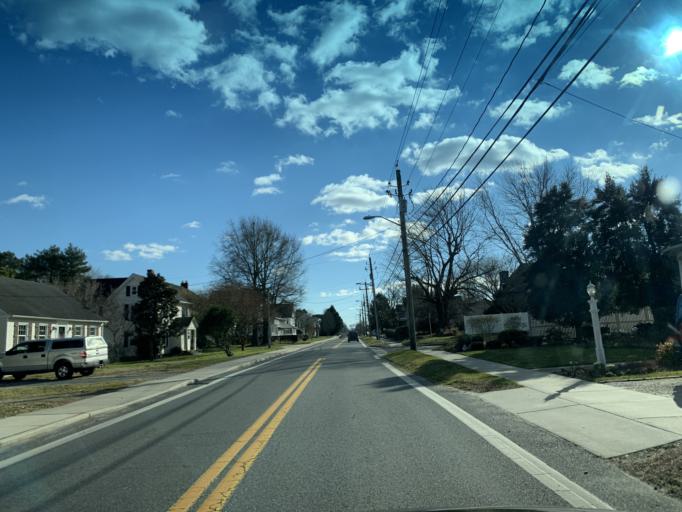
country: US
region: Maryland
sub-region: Worcester County
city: Berlin
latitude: 38.3333
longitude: -75.2209
